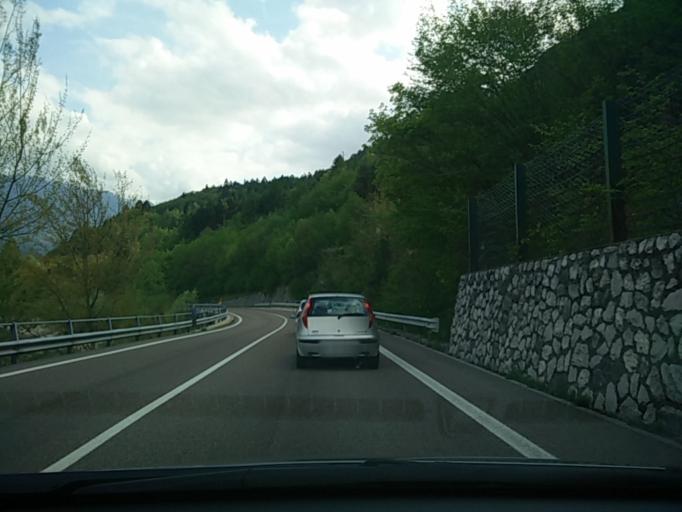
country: IT
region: Veneto
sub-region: Provincia di Belluno
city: Farra d'Alpago
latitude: 46.1123
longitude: 12.3260
